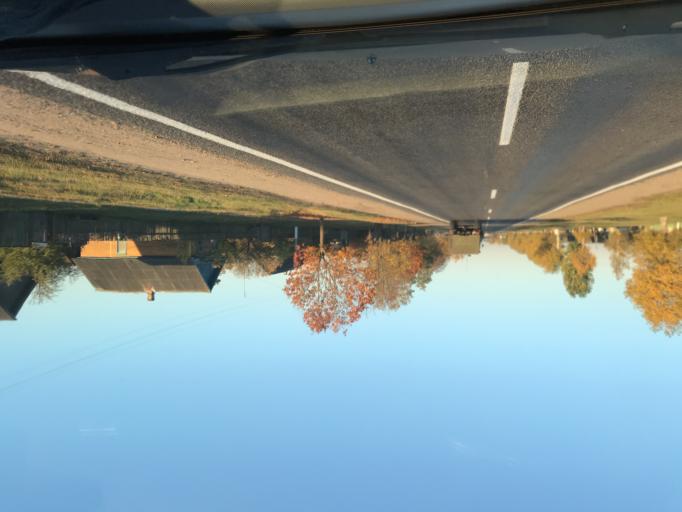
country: BY
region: Minsk
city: Staryya Darohi
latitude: 53.0458
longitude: 28.1112
